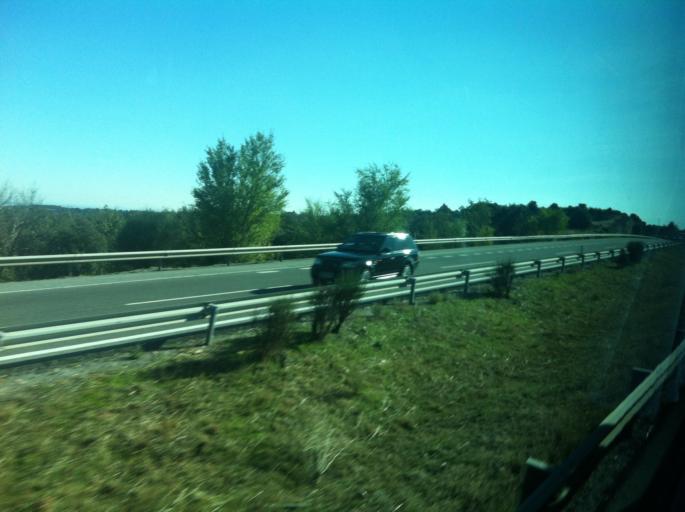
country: ES
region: Madrid
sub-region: Provincia de Madrid
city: La Cabrera
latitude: 40.8578
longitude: -3.6099
